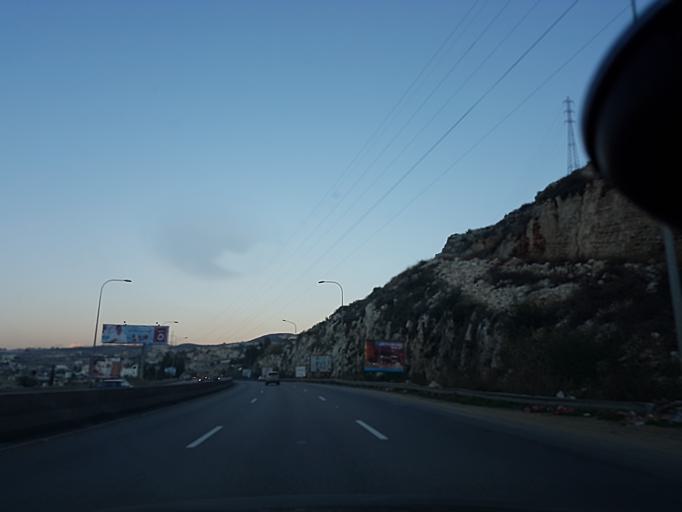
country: LB
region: Liban-Sud
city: Sidon
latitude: 33.6509
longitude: 35.4175
